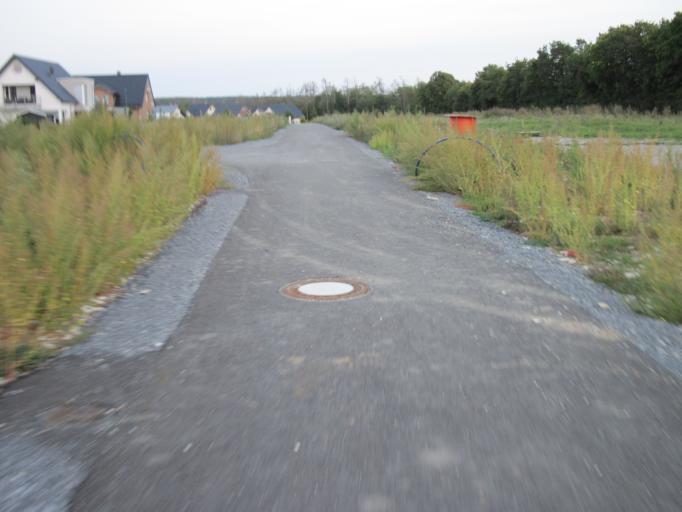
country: DE
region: North Rhine-Westphalia
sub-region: Regierungsbezirk Detmold
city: Salzkotten
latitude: 51.6303
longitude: 8.6665
